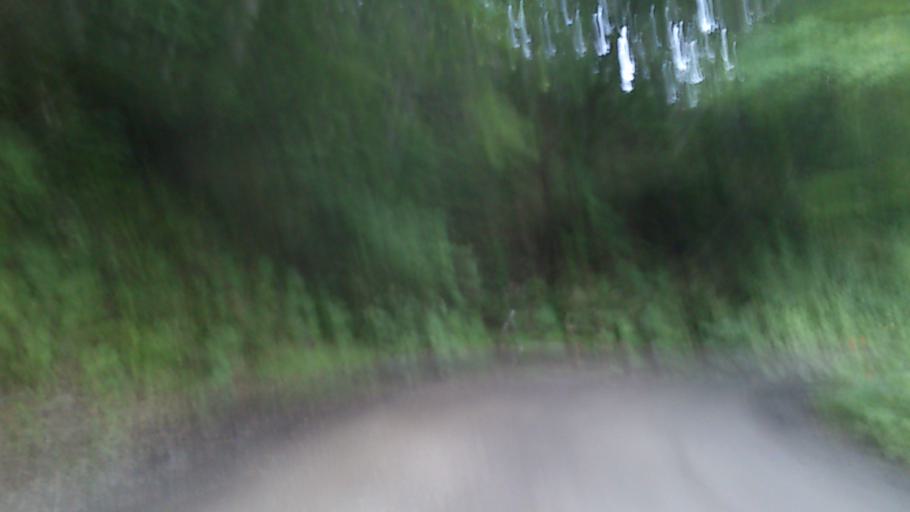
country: JP
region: Aomori
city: Hirosaki
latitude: 40.5362
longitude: 140.1844
